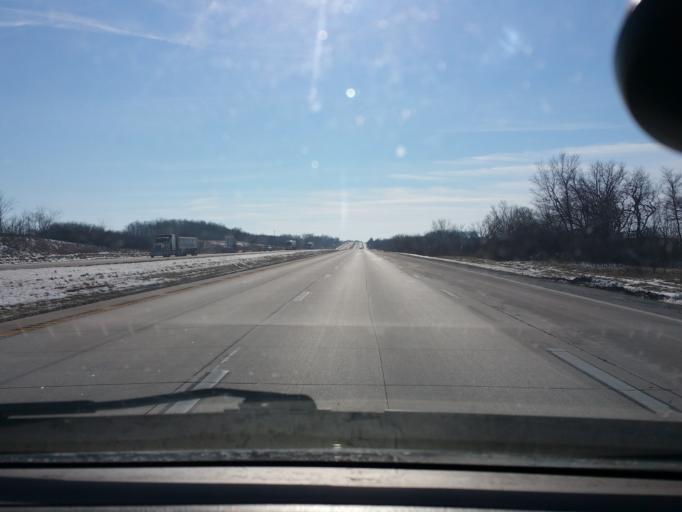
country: US
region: Missouri
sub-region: Daviess County
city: Gallatin
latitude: 39.9937
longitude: -94.0957
